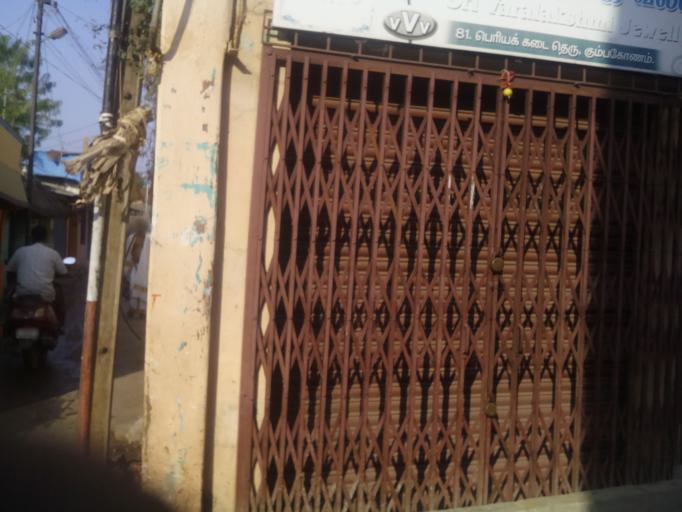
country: IN
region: Tamil Nadu
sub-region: Thanjavur
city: Kumbakonam
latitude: 10.9603
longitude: 79.3732
